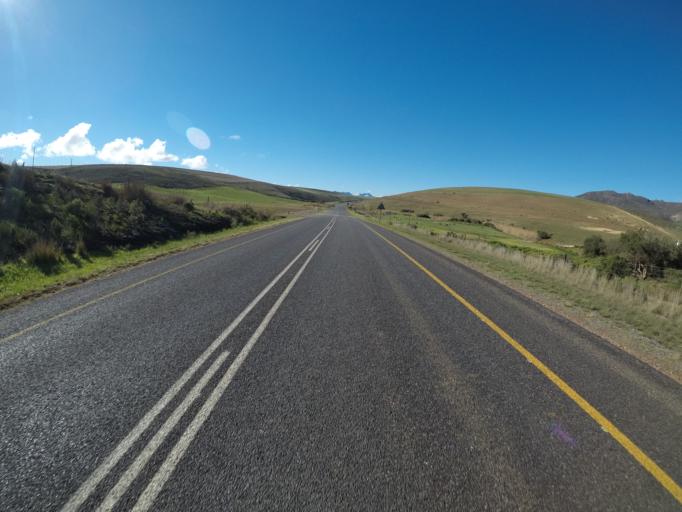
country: ZA
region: Western Cape
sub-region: Overberg District Municipality
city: Caledon
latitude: -34.1567
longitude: 19.4557
